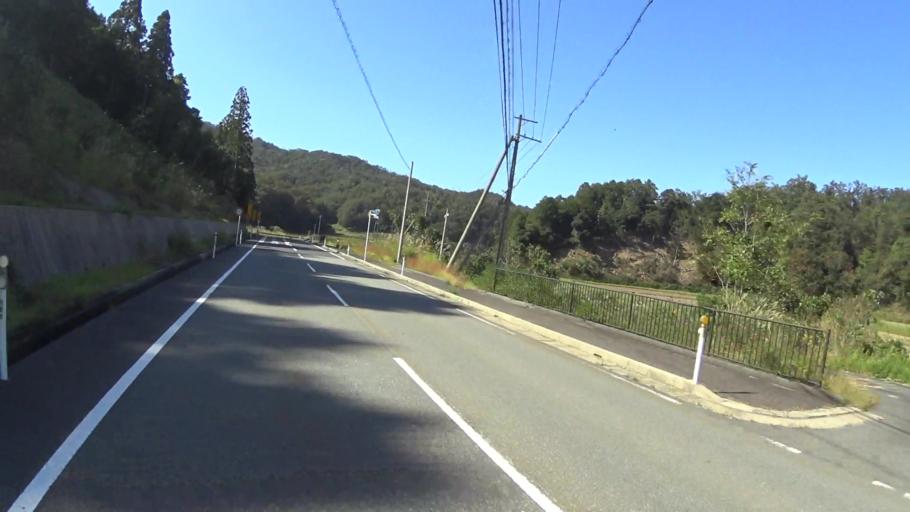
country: JP
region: Hyogo
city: Toyooka
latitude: 35.5652
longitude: 134.9766
